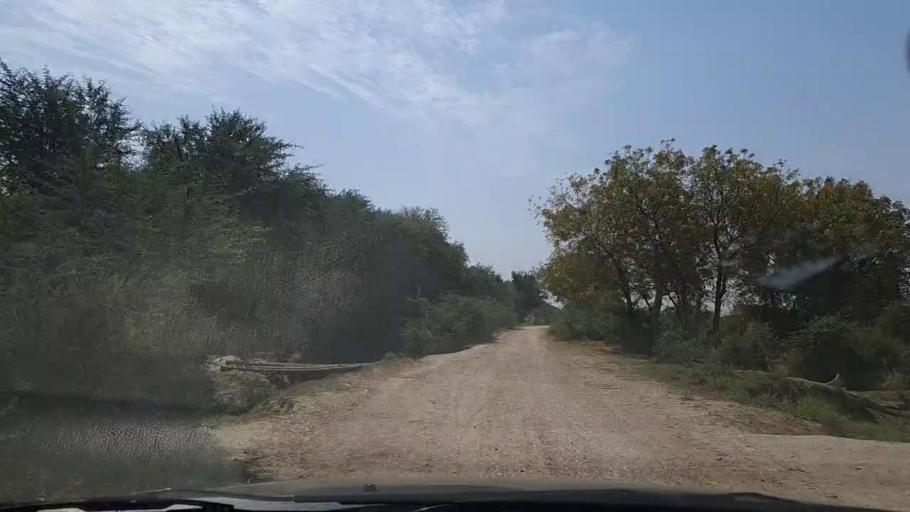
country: PK
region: Sindh
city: Mirpur Batoro
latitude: 24.6463
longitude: 68.1511
